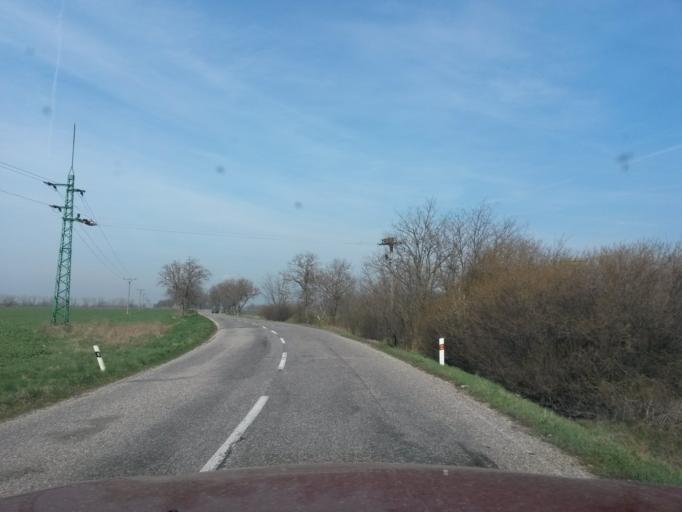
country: SK
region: Nitriansky
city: Levice
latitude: 48.1360
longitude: 18.5912
